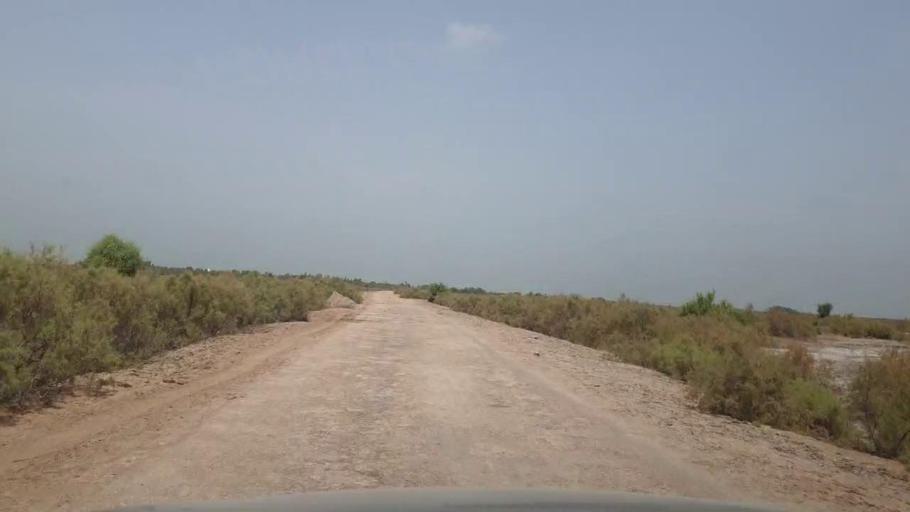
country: PK
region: Sindh
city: Garhi Yasin
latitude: 27.9142
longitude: 68.3791
